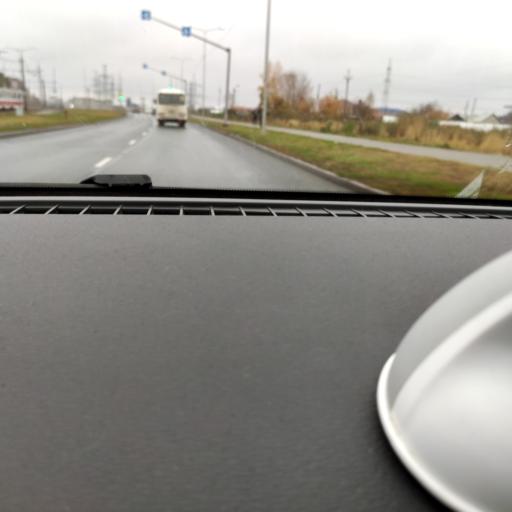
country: RU
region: Samara
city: Samara
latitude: 53.2669
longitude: 50.2290
